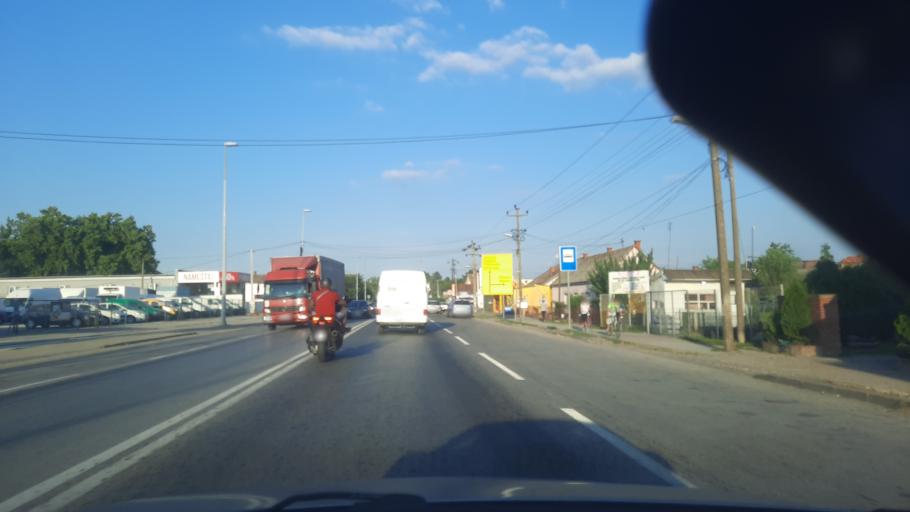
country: RS
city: Jelenca
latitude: 44.7387
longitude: 19.7320
